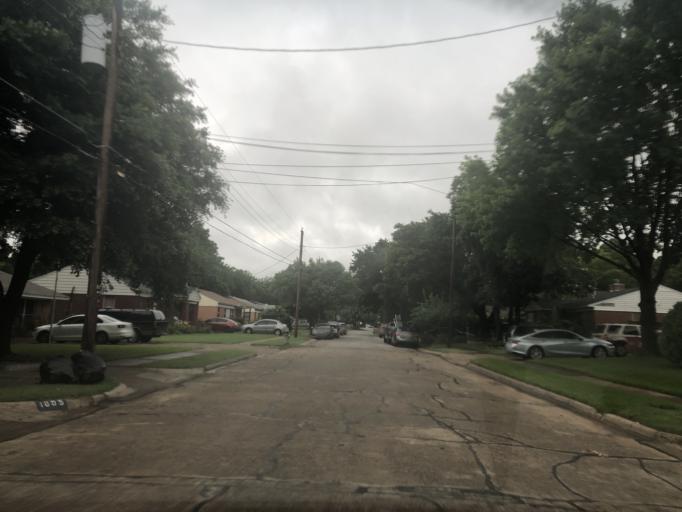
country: US
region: Texas
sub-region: Dallas County
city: Irving
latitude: 32.7959
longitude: -96.9497
